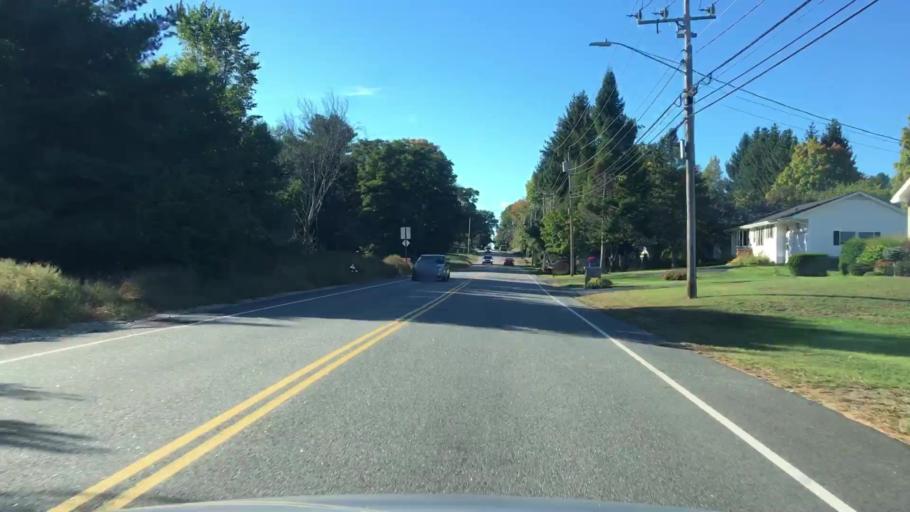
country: US
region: Maine
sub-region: Androscoggin County
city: Lewiston
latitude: 44.0812
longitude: -70.1685
